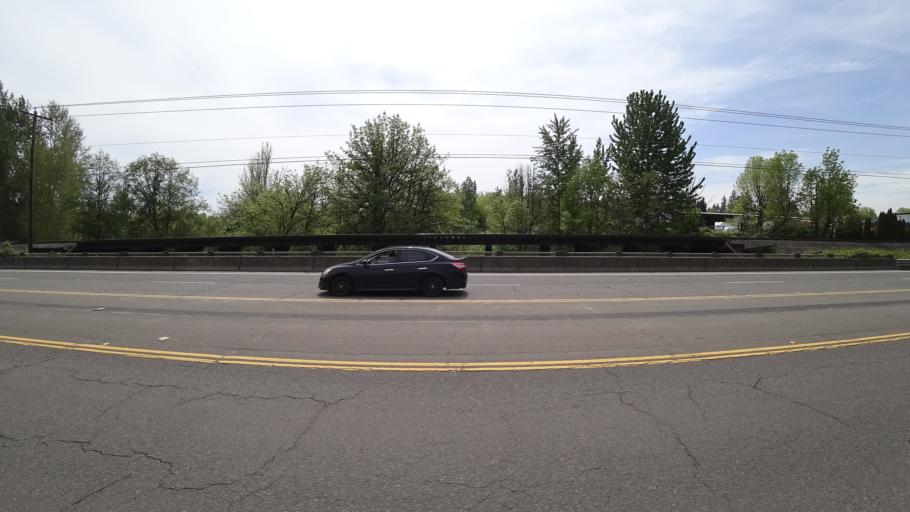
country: US
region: Oregon
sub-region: Washington County
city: Hillsboro
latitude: 45.5022
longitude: -122.9475
